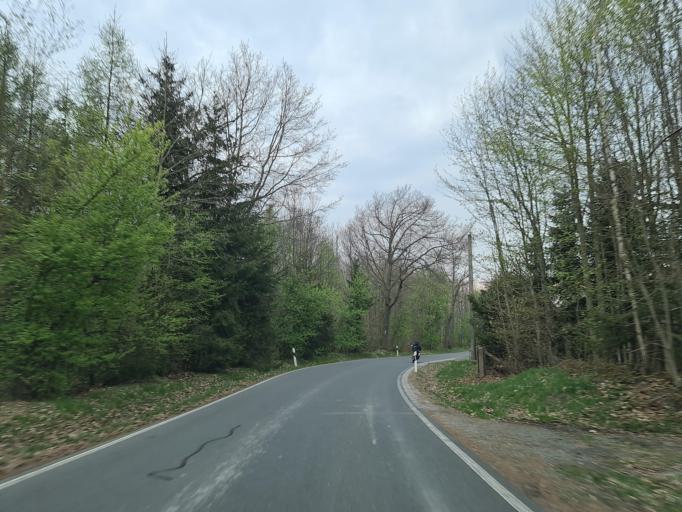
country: DE
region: Saxony
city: Ellefeld
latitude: 50.4655
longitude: 12.3925
